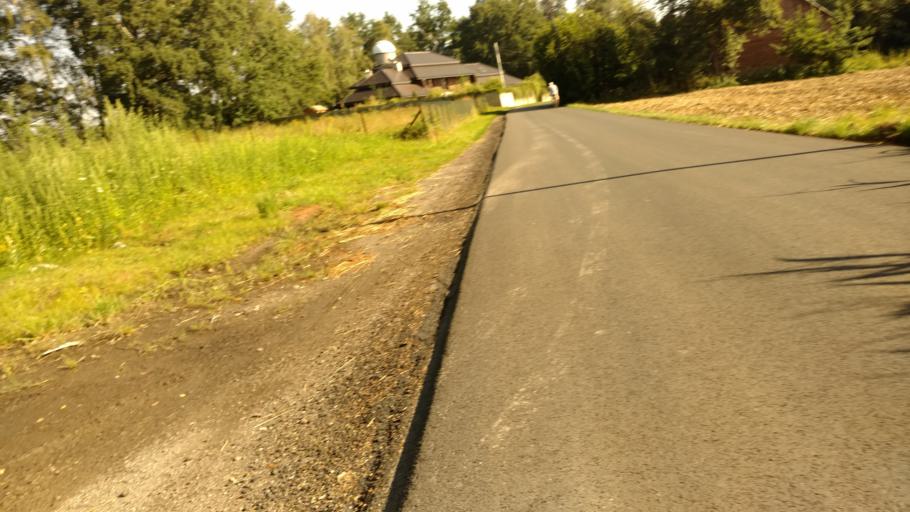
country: PL
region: Silesian Voivodeship
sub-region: Powiat pszczynski
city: Jankowice
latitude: 49.9917
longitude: 19.0091
